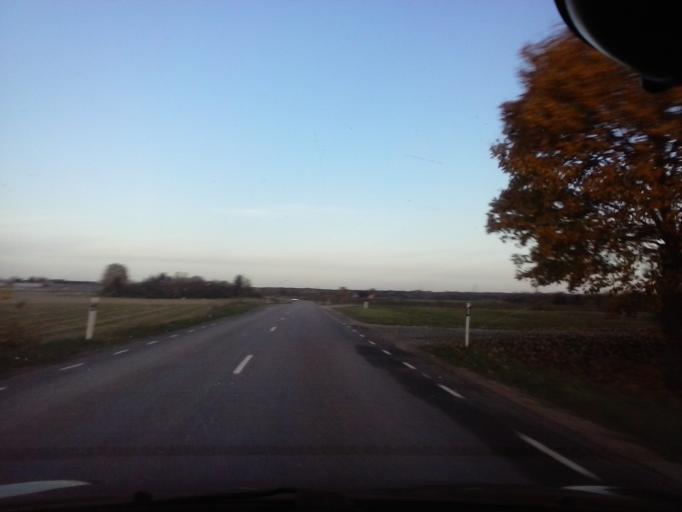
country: EE
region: Harju
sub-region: Nissi vald
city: Turba
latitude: 58.9084
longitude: 24.1330
